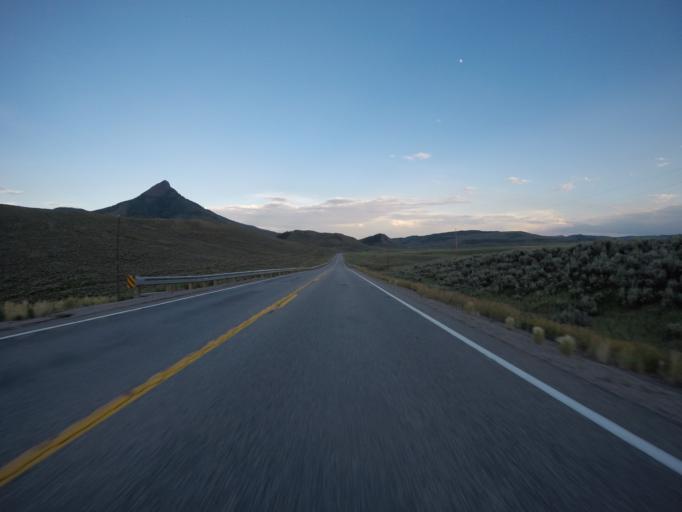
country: US
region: Colorado
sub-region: Grand County
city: Kremmling
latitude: 40.3253
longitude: -106.5288
